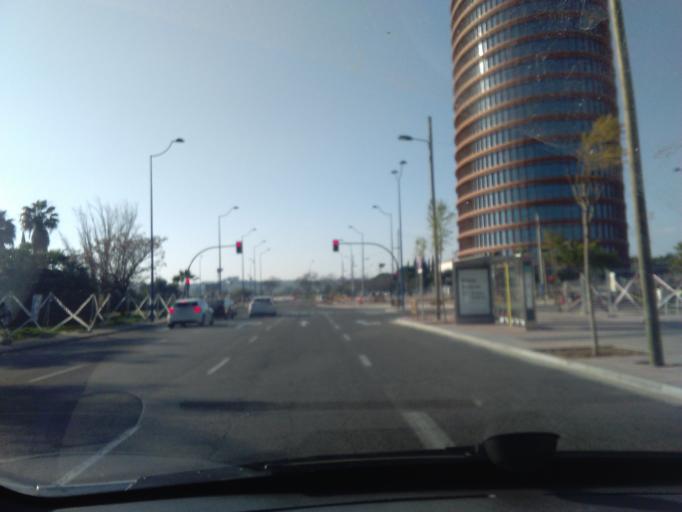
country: ES
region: Andalusia
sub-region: Provincia de Sevilla
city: Camas
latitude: 37.3906
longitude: -6.0089
